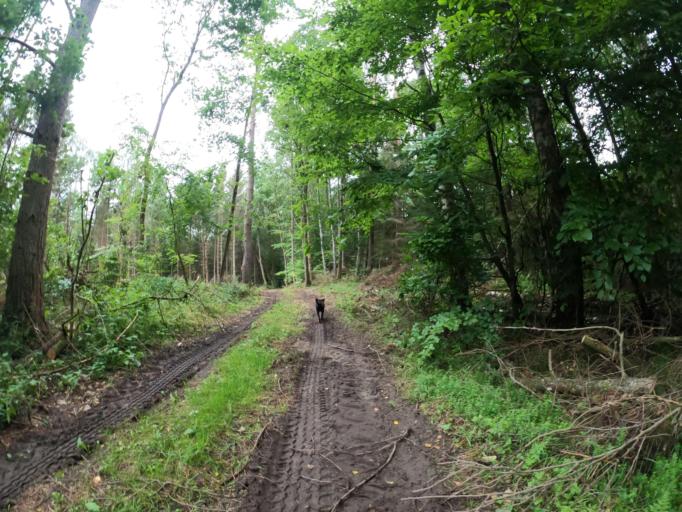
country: PL
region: West Pomeranian Voivodeship
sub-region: Powiat szczecinecki
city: Grzmiaca
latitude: 53.9715
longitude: 16.4414
